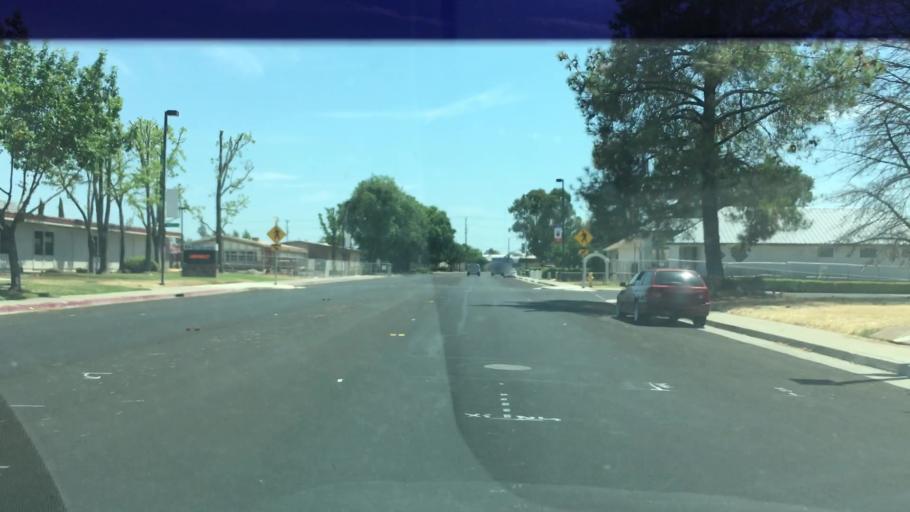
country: US
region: California
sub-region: Sacramento County
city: Galt
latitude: 38.2571
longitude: -121.3004
